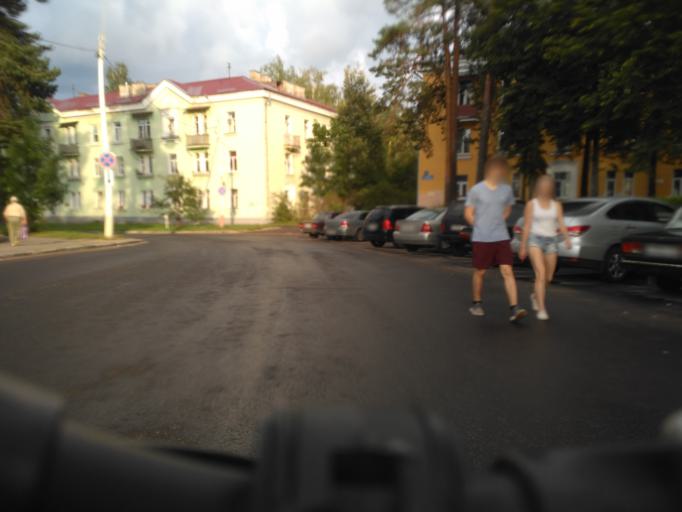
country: RU
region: Moskovskaya
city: Dubna
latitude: 56.7456
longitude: 37.1954
